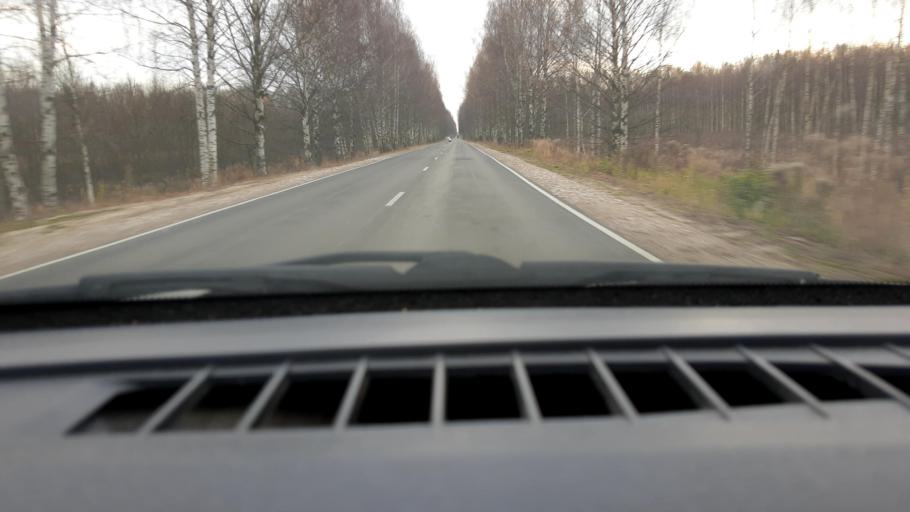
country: RU
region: Nizjnij Novgorod
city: Neklyudovo
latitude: 56.4860
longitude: 43.8654
